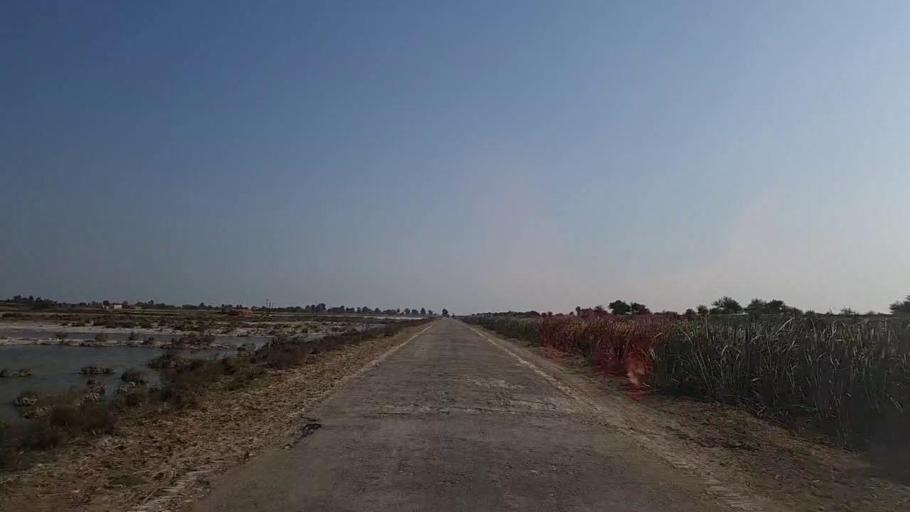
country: PK
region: Sindh
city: Sanghar
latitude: 25.9777
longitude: 69.0260
